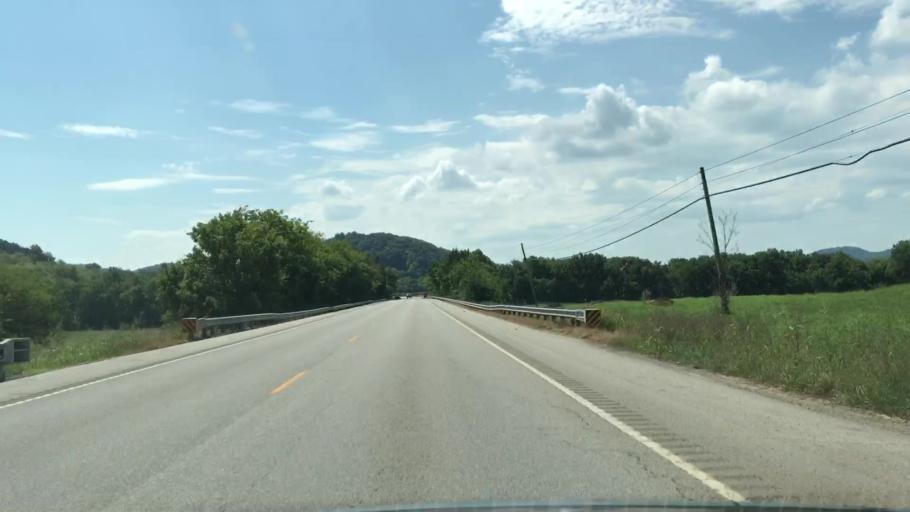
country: US
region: Tennessee
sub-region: Smith County
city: Carthage
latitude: 36.3113
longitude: -86.0086
